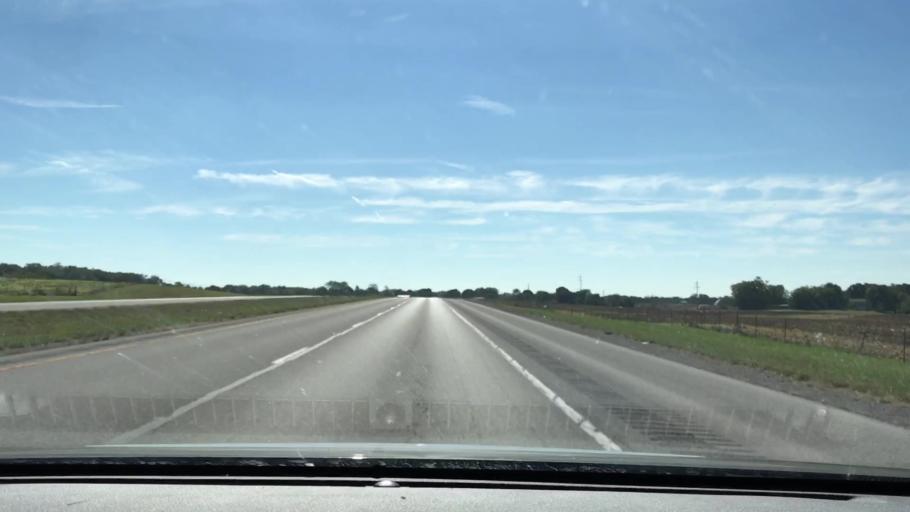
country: US
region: Kentucky
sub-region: Todd County
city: Elkton
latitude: 36.8161
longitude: -87.1416
